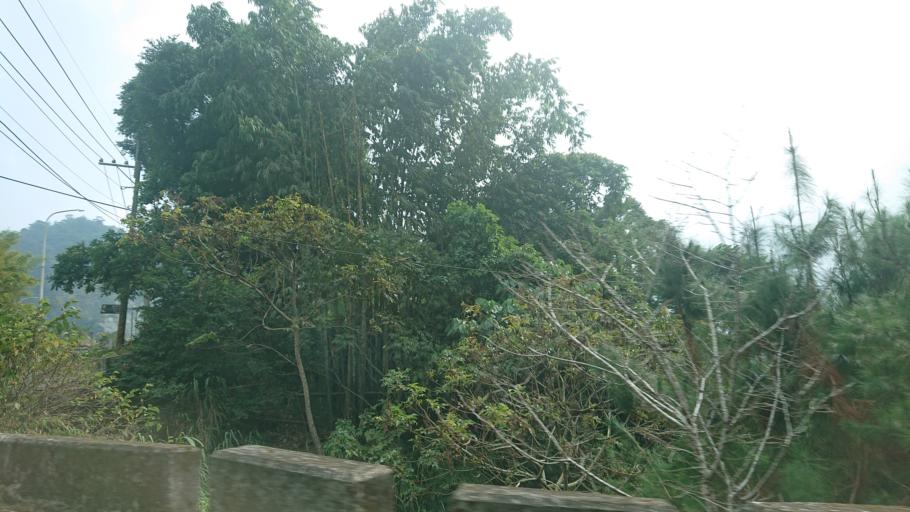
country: TW
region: Taiwan
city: Lugu
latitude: 23.5948
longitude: 120.7002
